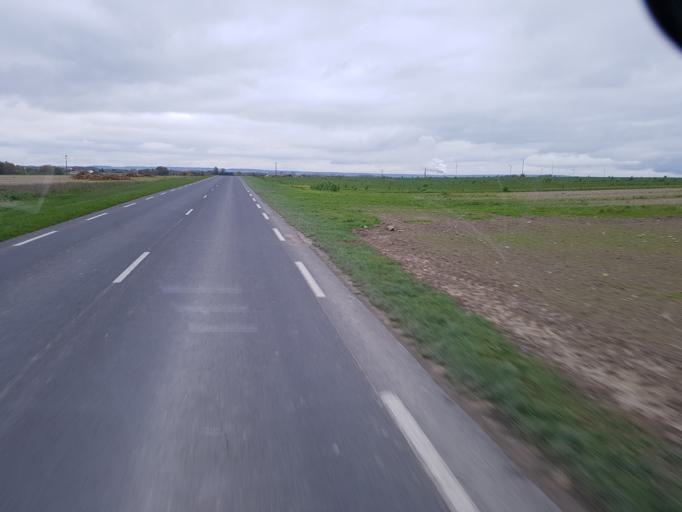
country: FR
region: Champagne-Ardenne
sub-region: Departement de la Marne
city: Saint-Just-Sauvage
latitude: 48.5844
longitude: 3.8432
